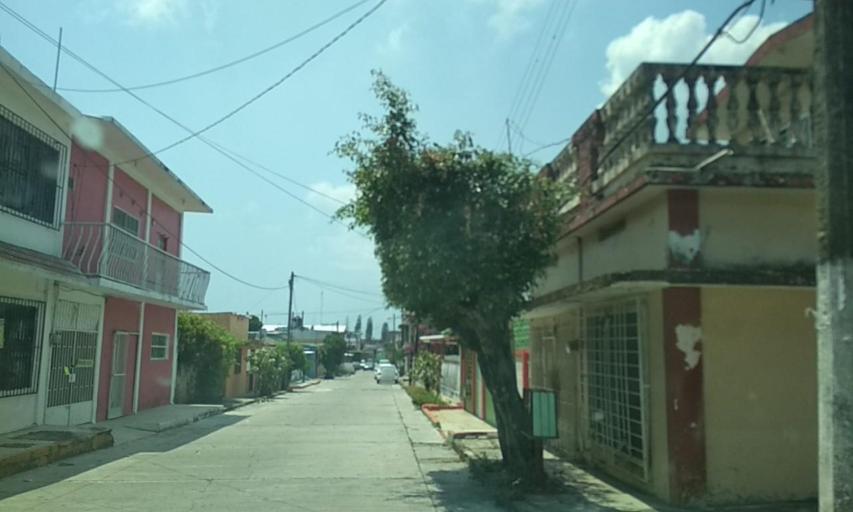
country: MX
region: Veracruz
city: Las Choapas
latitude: 17.9121
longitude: -94.0917
